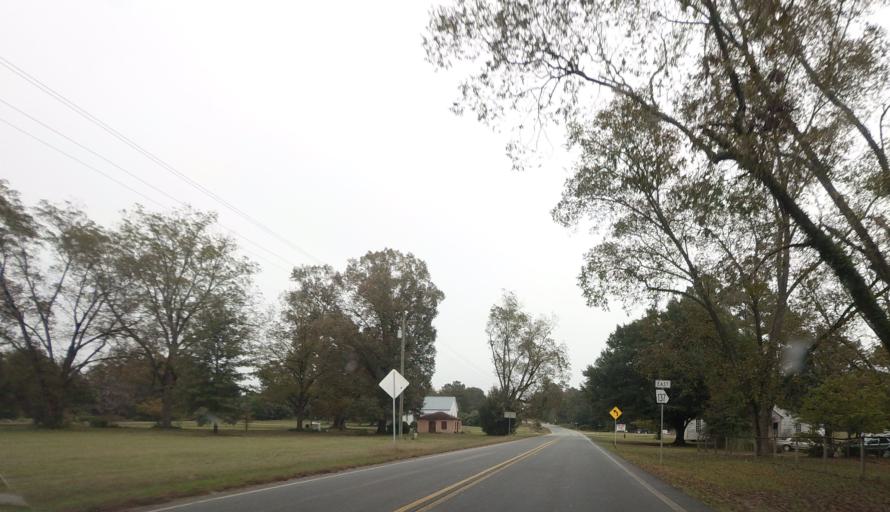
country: US
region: Georgia
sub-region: Marion County
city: Buena Vista
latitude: 32.3808
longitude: -84.4387
